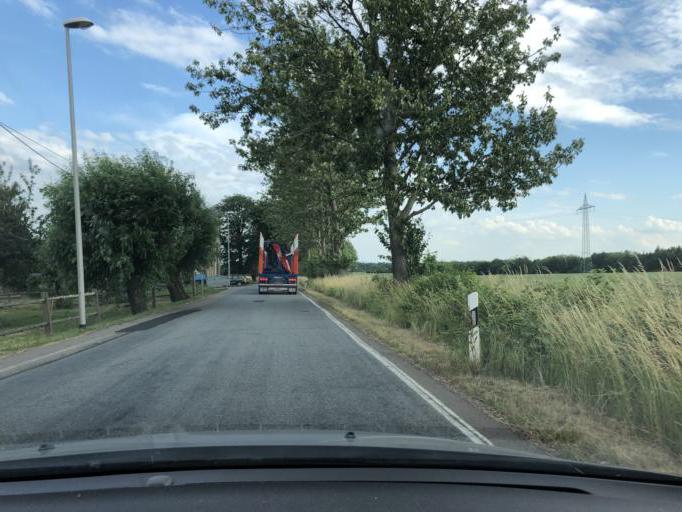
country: DE
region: Saxony
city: Freital
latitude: 51.0535
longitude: 13.6072
